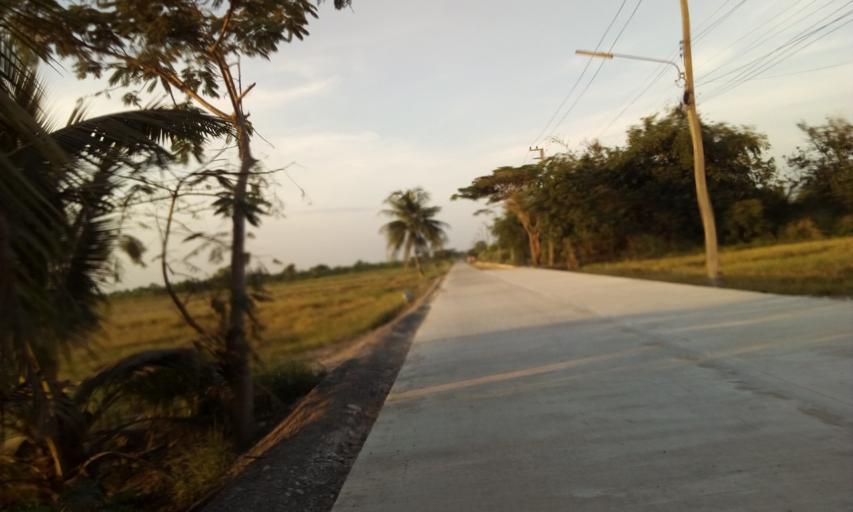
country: TH
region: Pathum Thani
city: Nong Suea
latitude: 14.0400
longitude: 100.8665
